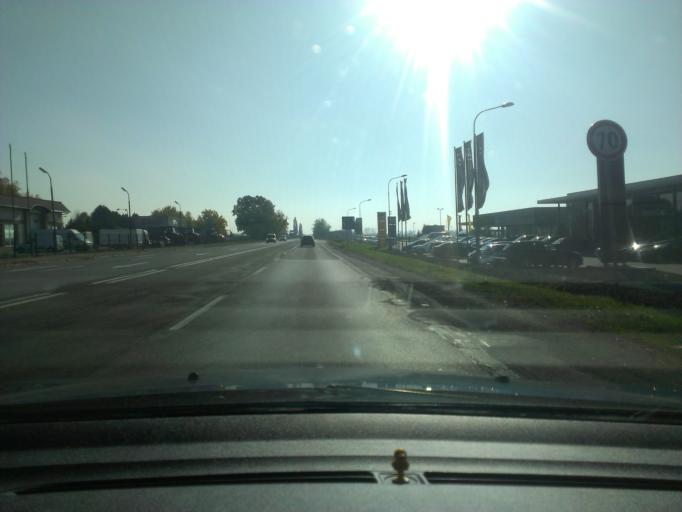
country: SK
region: Nitriansky
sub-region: Okres Nove Zamky
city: Nove Zamky
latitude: 47.9676
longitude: 18.1842
